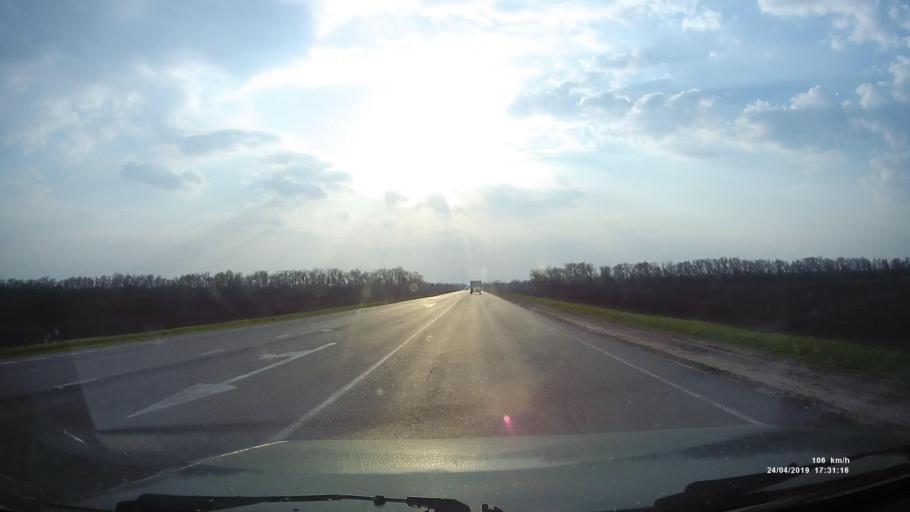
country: RU
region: Rostov
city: Tselina
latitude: 46.5228
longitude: 41.1236
